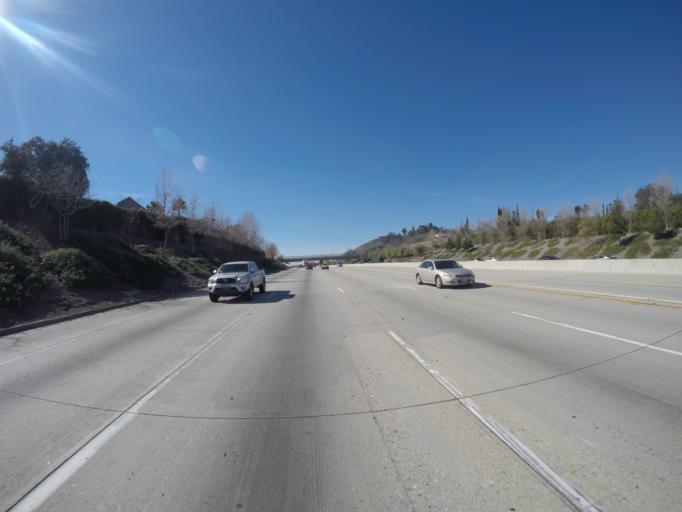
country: US
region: California
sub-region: Los Angeles County
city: Claremont
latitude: 34.1203
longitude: -117.7381
